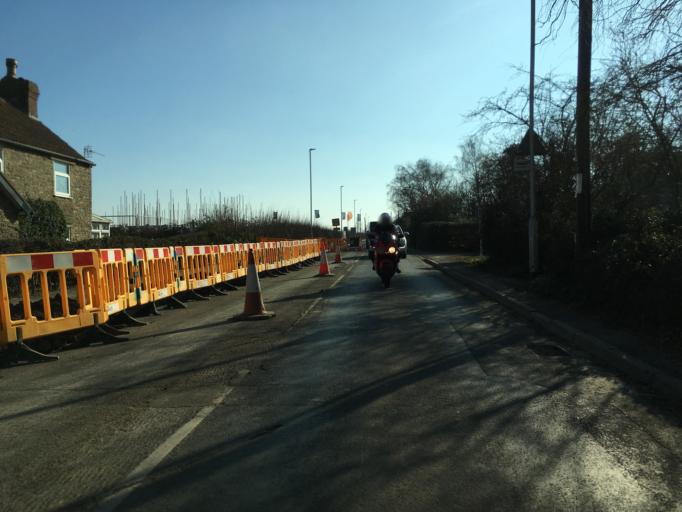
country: GB
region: England
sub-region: South Gloucestershire
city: Wickwar
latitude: 51.5882
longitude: -2.3983
